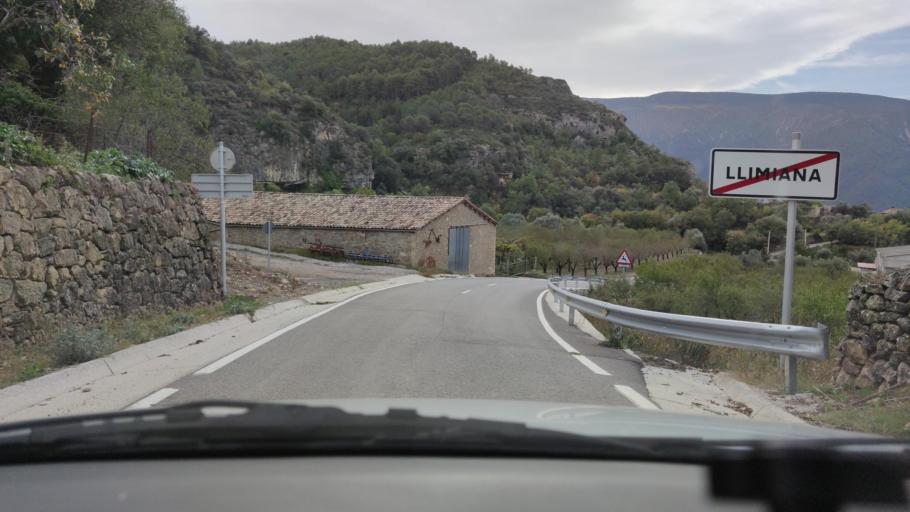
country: ES
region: Catalonia
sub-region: Provincia de Lleida
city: Llimiana
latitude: 42.0745
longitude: 0.9173
